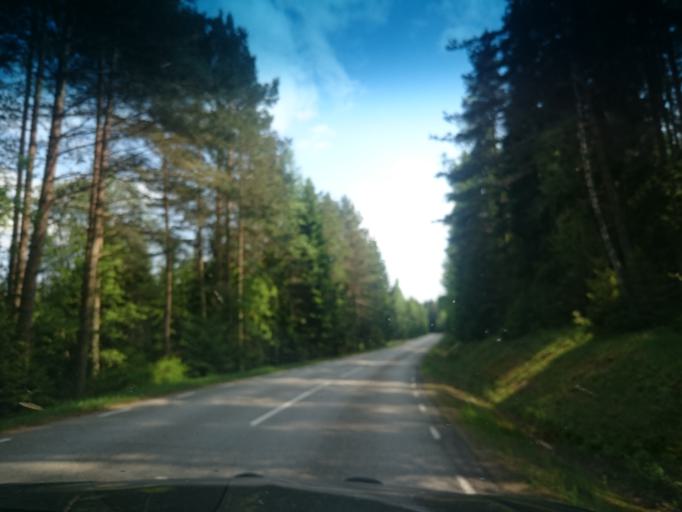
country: SE
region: Joenkoeping
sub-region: Vetlanda Kommun
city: Vetlanda
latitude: 57.3722
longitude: 15.0522
